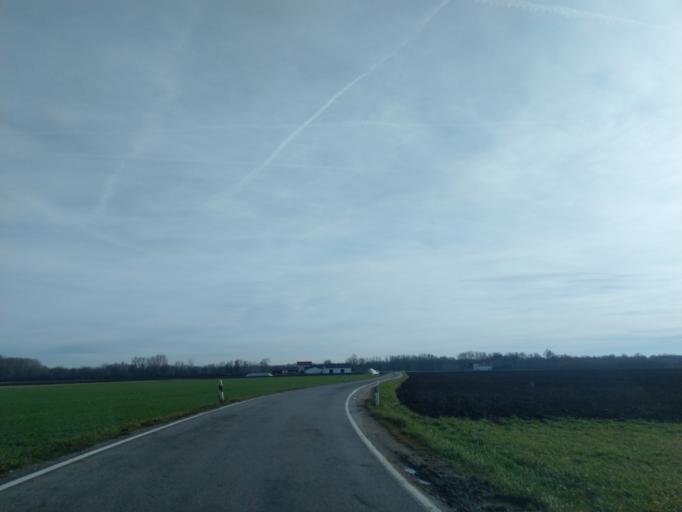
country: DE
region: Bavaria
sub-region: Lower Bavaria
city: Oberporing
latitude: 48.7298
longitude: 12.8266
